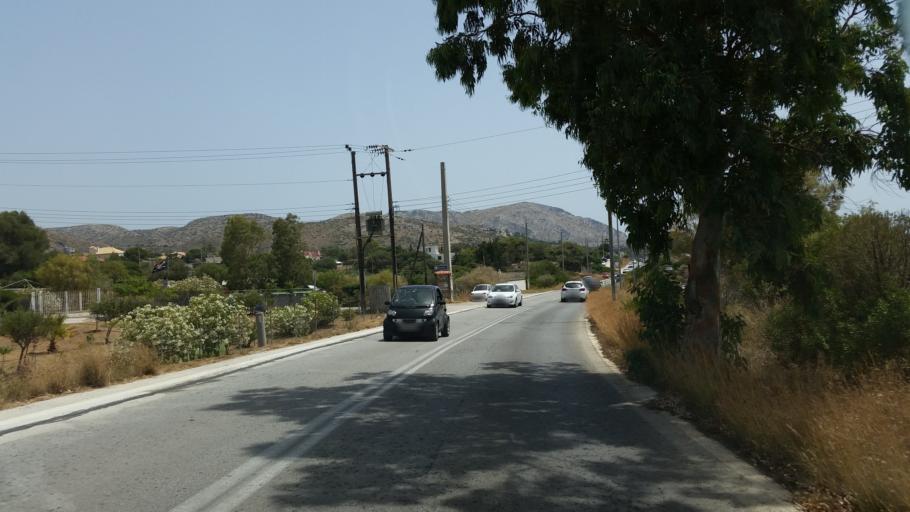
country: GR
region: Attica
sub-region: Nomarchia Anatolikis Attikis
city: Palaia Fokaia
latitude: 37.6974
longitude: 23.9383
